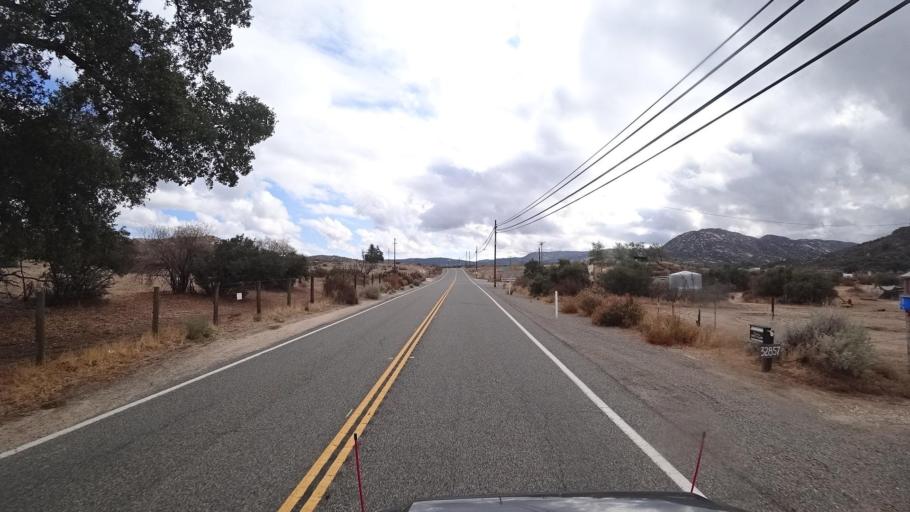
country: US
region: California
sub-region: San Diego County
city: Campo
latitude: 32.6301
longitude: -116.4421
